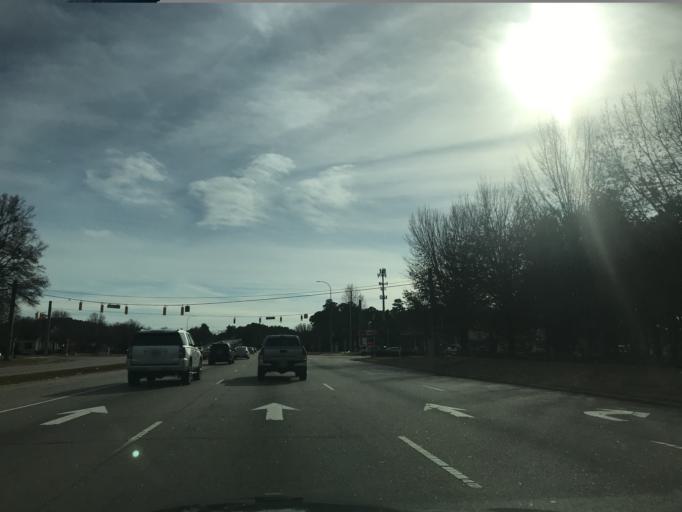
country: US
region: North Carolina
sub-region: Wake County
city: Raleigh
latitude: 35.8454
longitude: -78.5802
